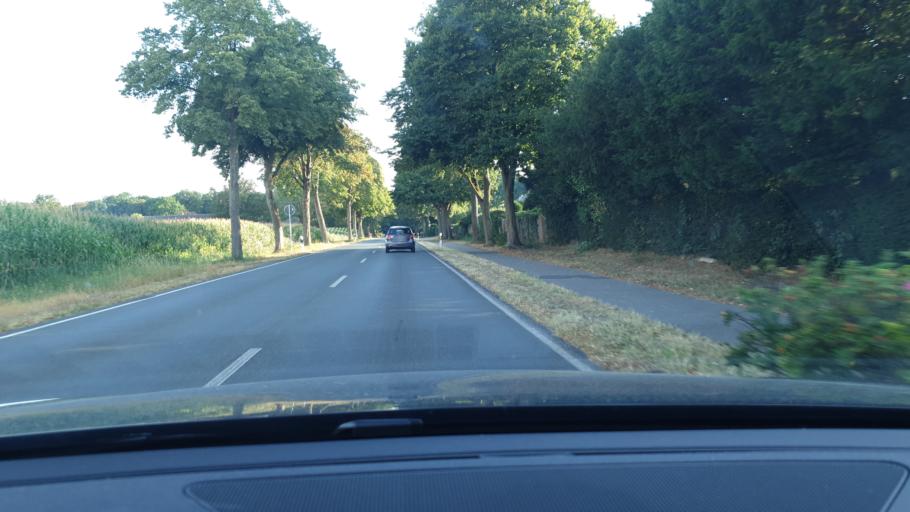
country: DE
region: North Rhine-Westphalia
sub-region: Regierungsbezirk Dusseldorf
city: Kleve
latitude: 51.7670
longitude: 6.1126
